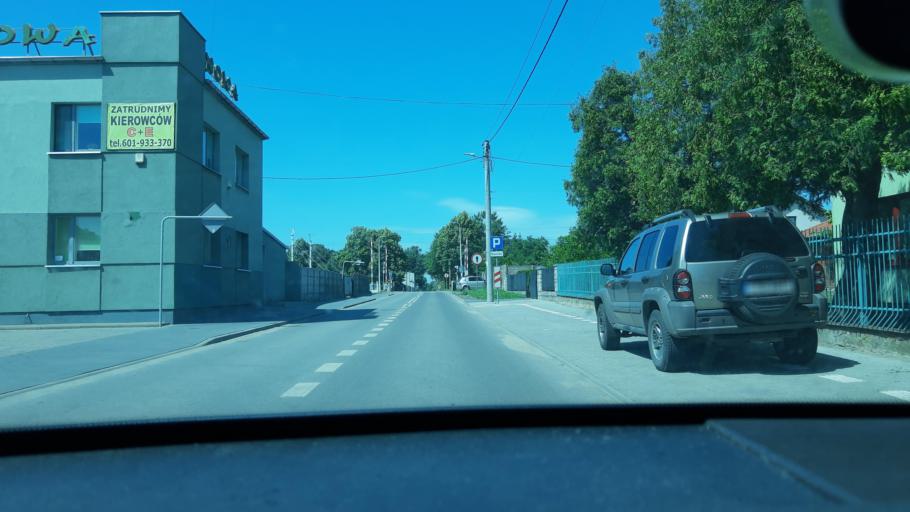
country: PL
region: Lodz Voivodeship
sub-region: Powiat zdunskowolski
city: Zdunska Wola
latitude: 51.6100
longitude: 18.9385
